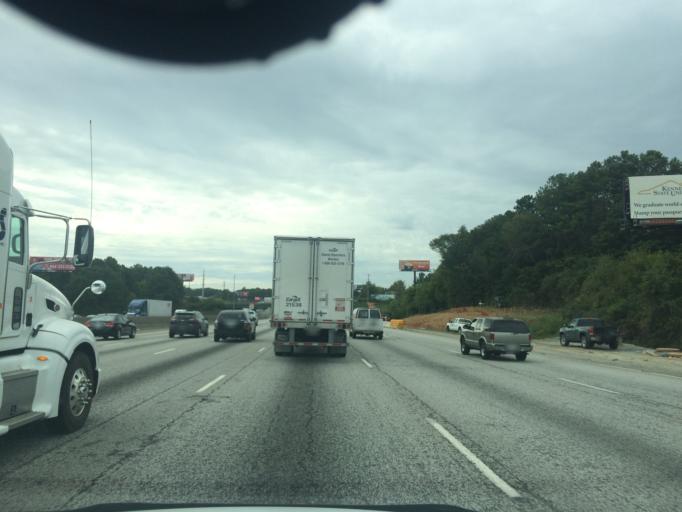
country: US
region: Georgia
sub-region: Cobb County
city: Marietta
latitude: 33.9753
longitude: -84.5333
